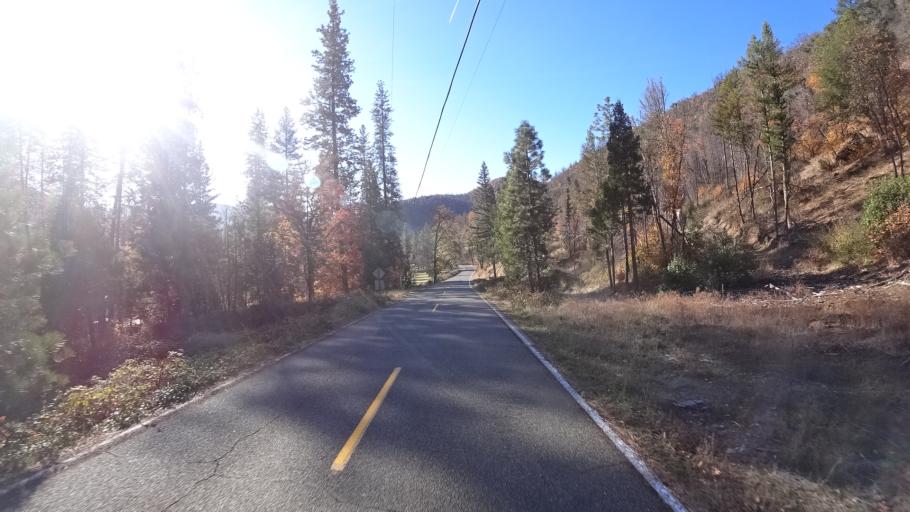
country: US
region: California
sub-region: Siskiyou County
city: Yreka
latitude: 41.8789
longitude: -122.8214
